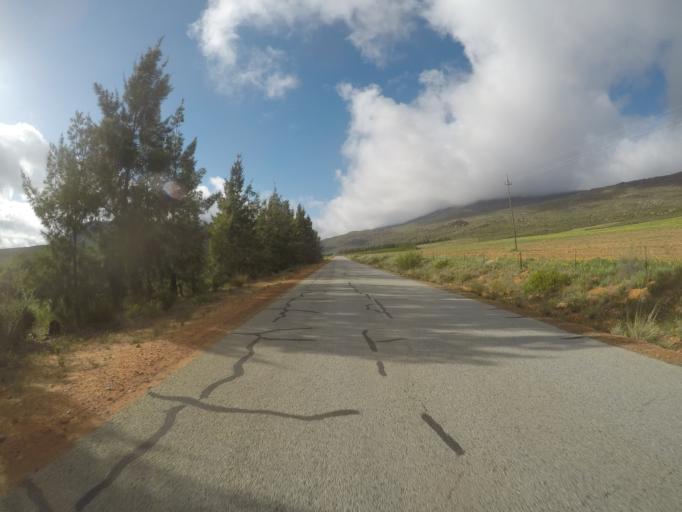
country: ZA
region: Western Cape
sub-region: West Coast District Municipality
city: Clanwilliam
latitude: -32.3513
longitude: 18.8482
